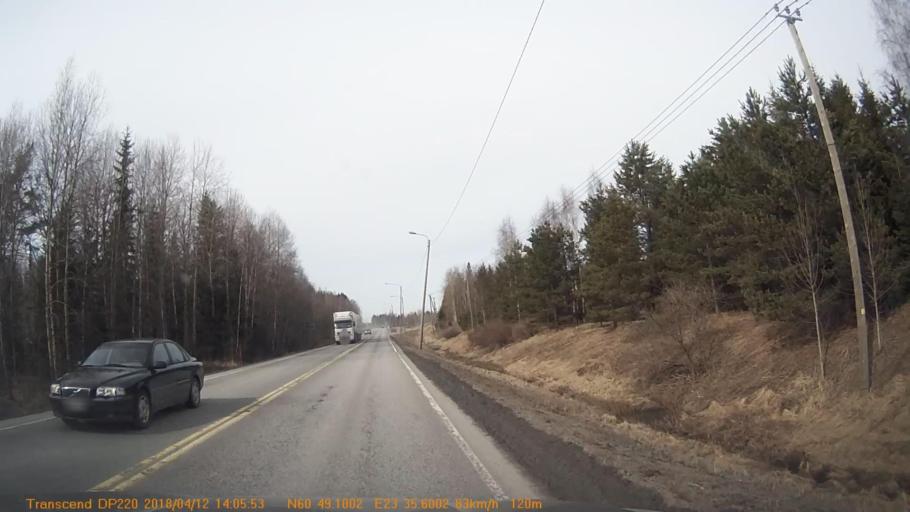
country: FI
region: Haeme
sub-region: Forssa
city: Forssa
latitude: 60.8186
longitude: 23.5931
